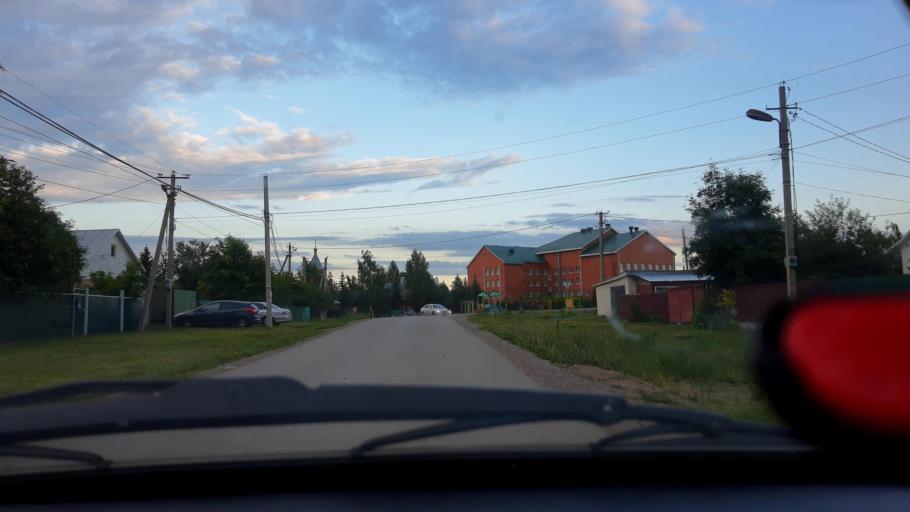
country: RU
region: Bashkortostan
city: Avdon
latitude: 54.4959
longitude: 55.8967
